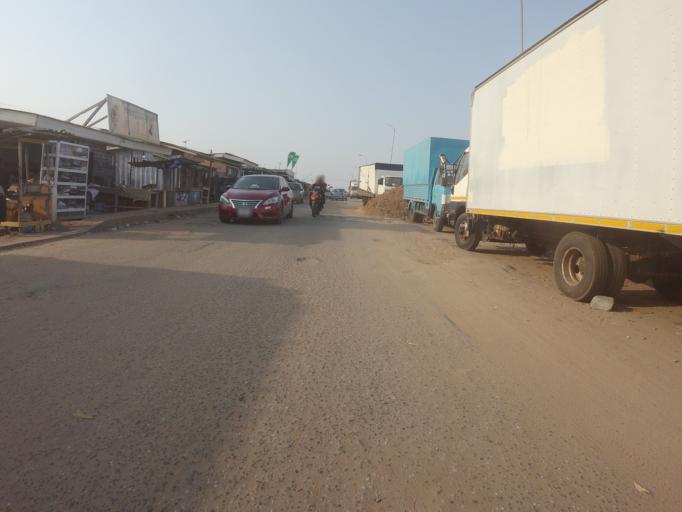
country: GH
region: Greater Accra
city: Nungua
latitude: 5.6124
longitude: -0.0465
